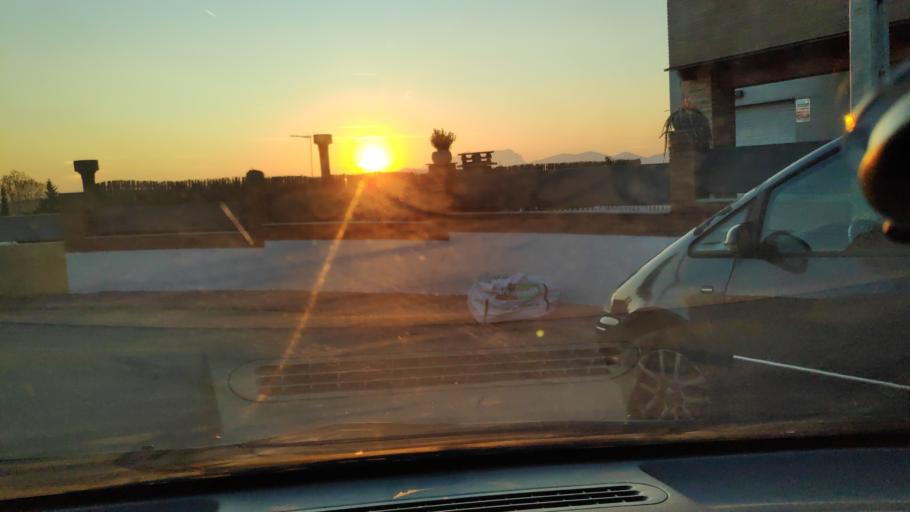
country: ES
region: Catalonia
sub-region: Provincia de Barcelona
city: Sant Quirze del Valles
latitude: 41.5323
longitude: 2.0498
